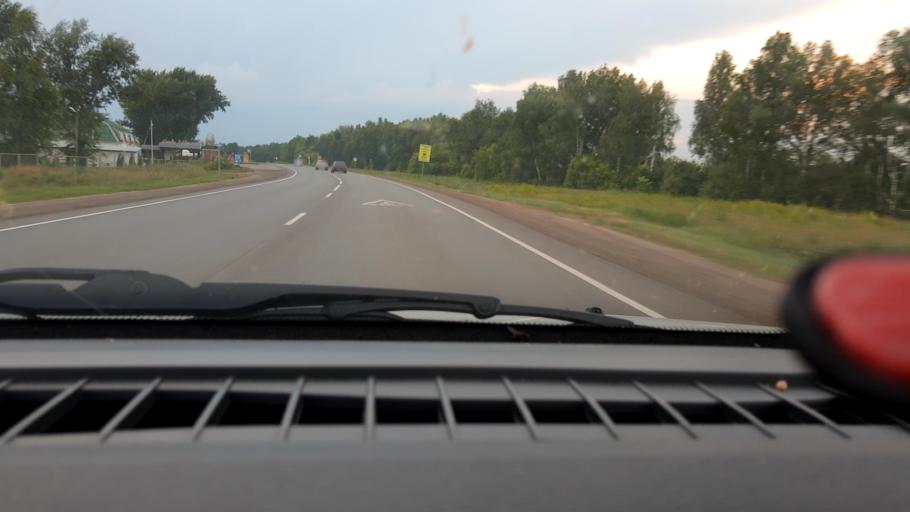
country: RU
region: Nizjnij Novgorod
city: Arzamas
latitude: 55.2960
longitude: 43.9370
